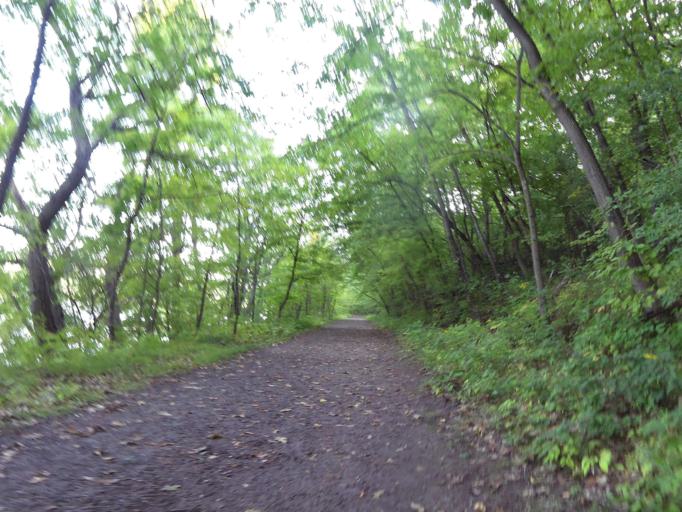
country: US
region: Minnesota
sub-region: Washington County
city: Afton
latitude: 44.8468
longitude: -92.7710
